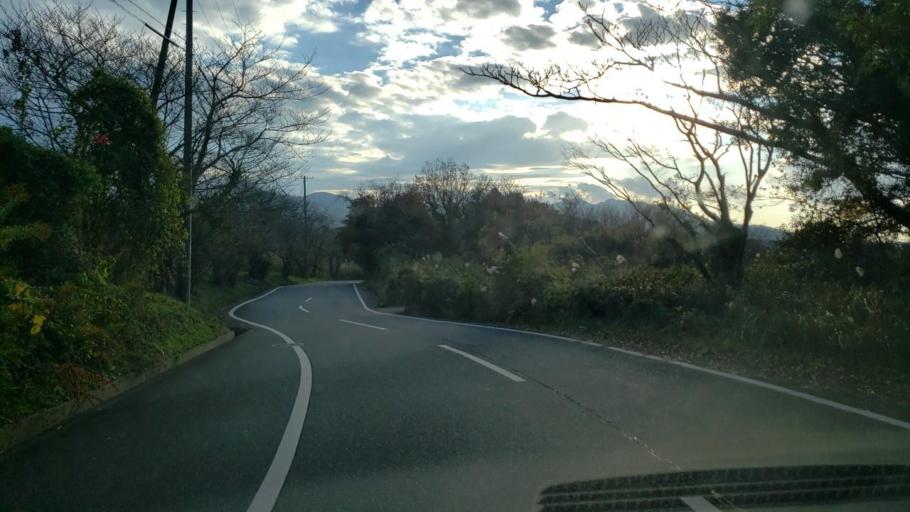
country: JP
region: Hyogo
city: Akashi
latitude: 34.5465
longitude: 134.9723
